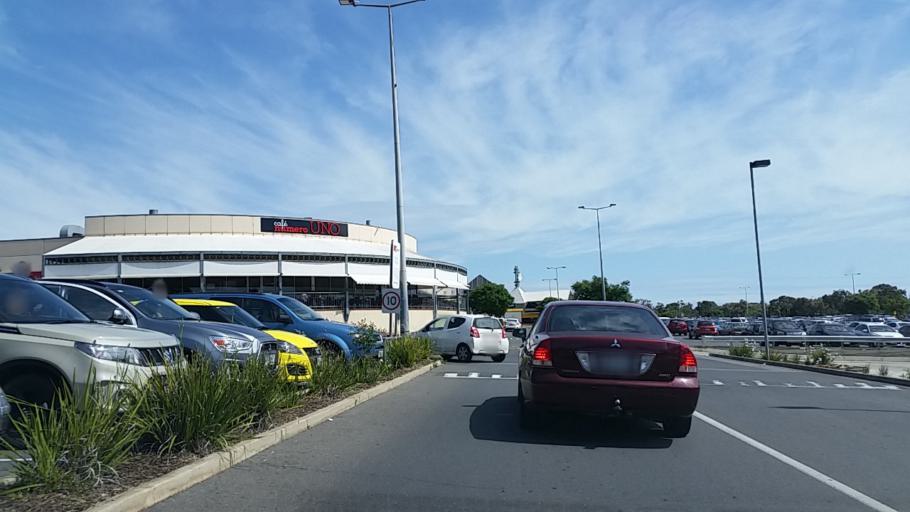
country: AU
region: South Australia
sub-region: Salisbury
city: Ingle Farm
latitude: -34.8281
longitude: 138.6482
